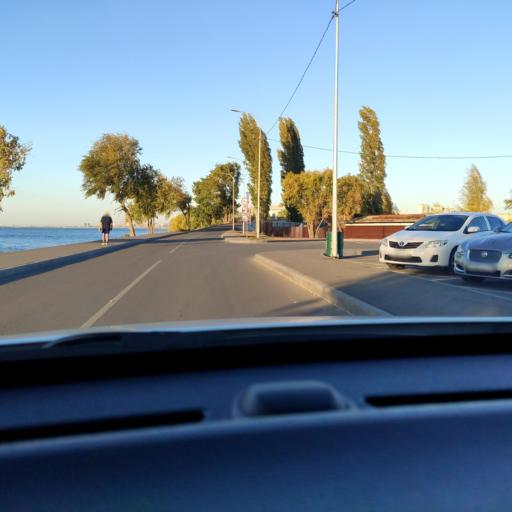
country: RU
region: Voronezj
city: Voronezh
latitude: 51.6685
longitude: 39.2277
